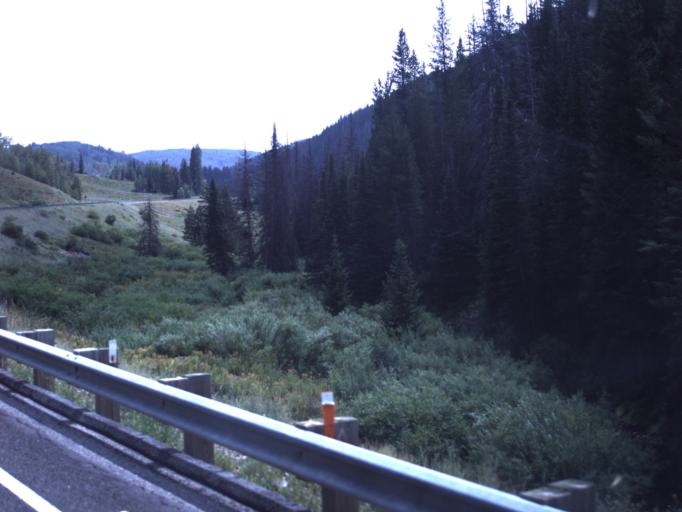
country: US
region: Utah
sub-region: Summit County
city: Francis
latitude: 40.5159
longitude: -111.0702
